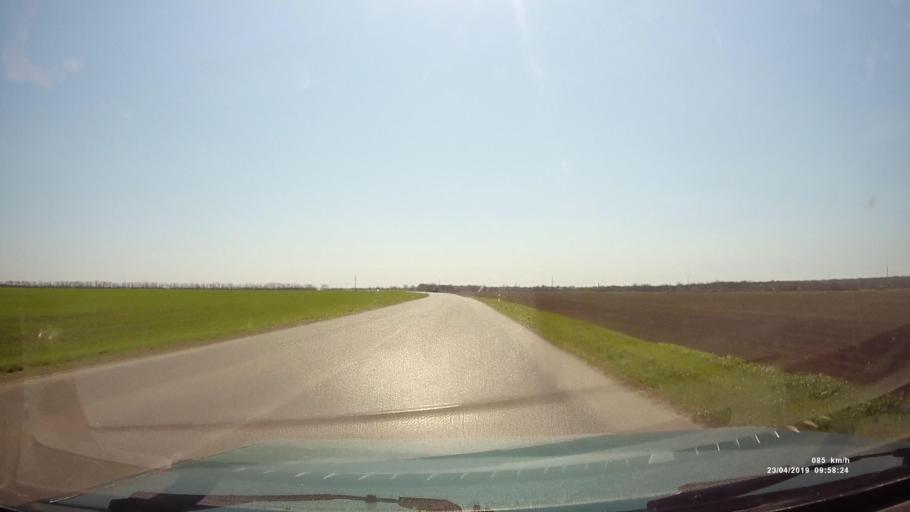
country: RU
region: Rostov
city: Sovetskoye
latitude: 46.7804
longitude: 42.0979
